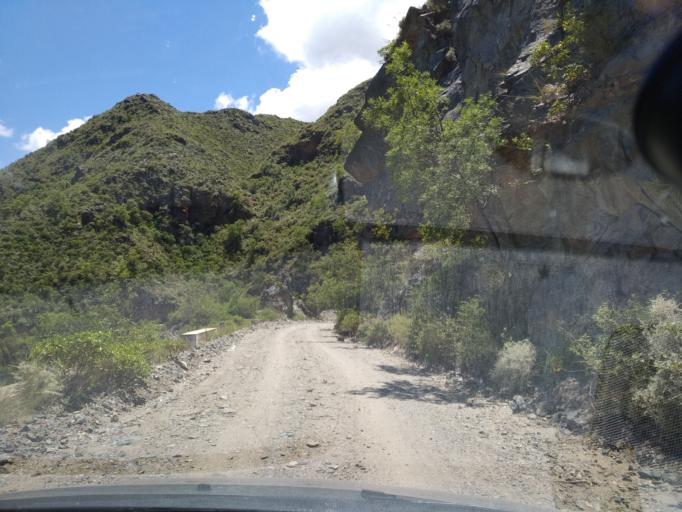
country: AR
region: Cordoba
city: Salsacate
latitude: -31.3727
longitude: -65.4067
